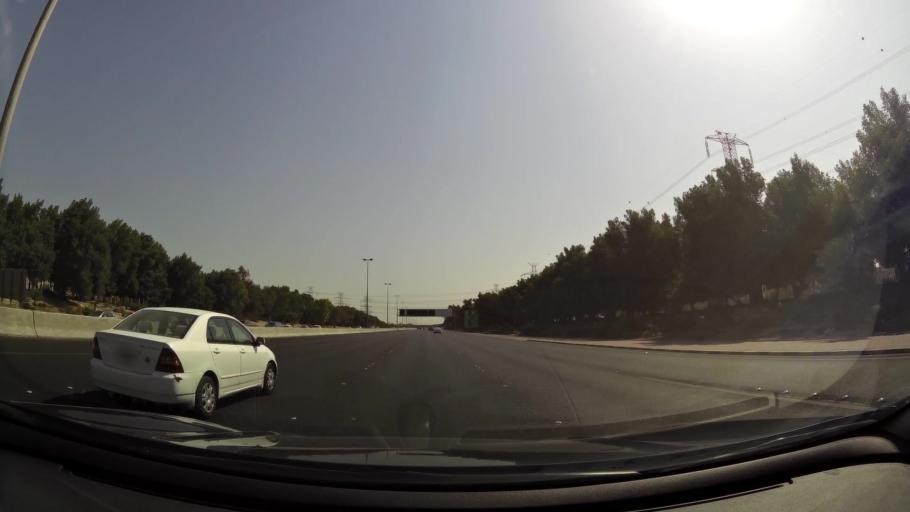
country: KW
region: Mubarak al Kabir
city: Sabah as Salim
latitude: 29.2758
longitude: 48.0369
